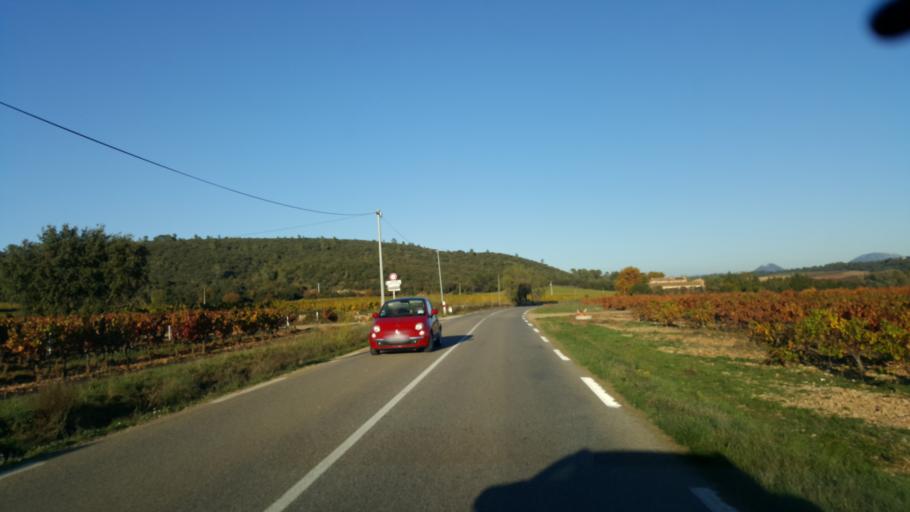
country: FR
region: Provence-Alpes-Cote d'Azur
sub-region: Departement du Var
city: Saint-Maximin-la-Sainte-Baume
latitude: 43.4990
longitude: 5.9002
